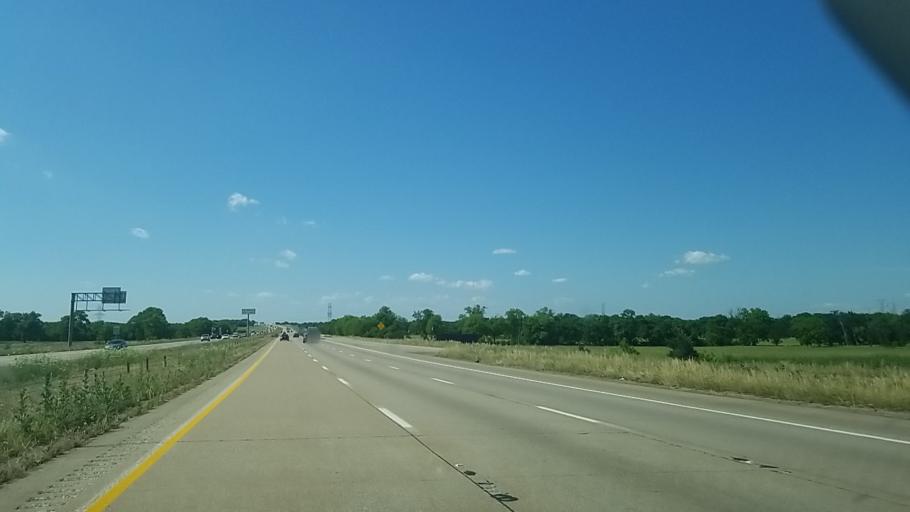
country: US
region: Texas
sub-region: Ellis County
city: Ferris
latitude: 32.5511
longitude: -96.6610
